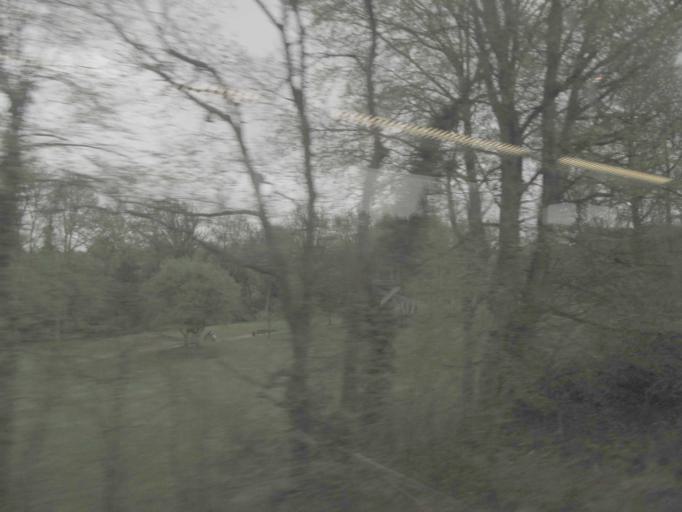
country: GB
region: England
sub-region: Bracknell Forest
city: Crowthorne
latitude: 51.3743
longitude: -0.8237
